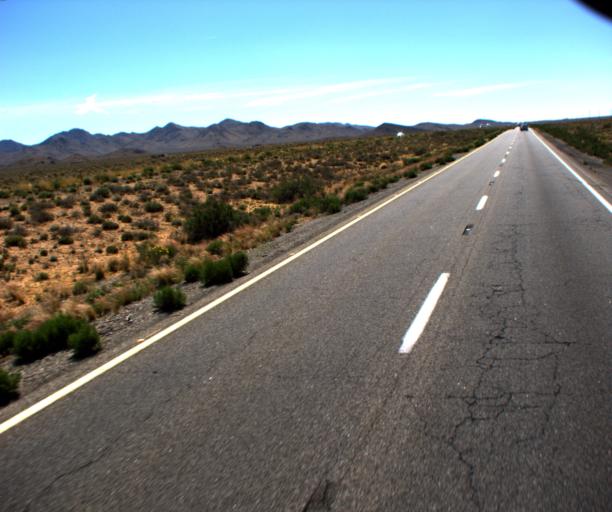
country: US
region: Arizona
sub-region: Mohave County
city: Dolan Springs
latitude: 35.4867
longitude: -114.3230
